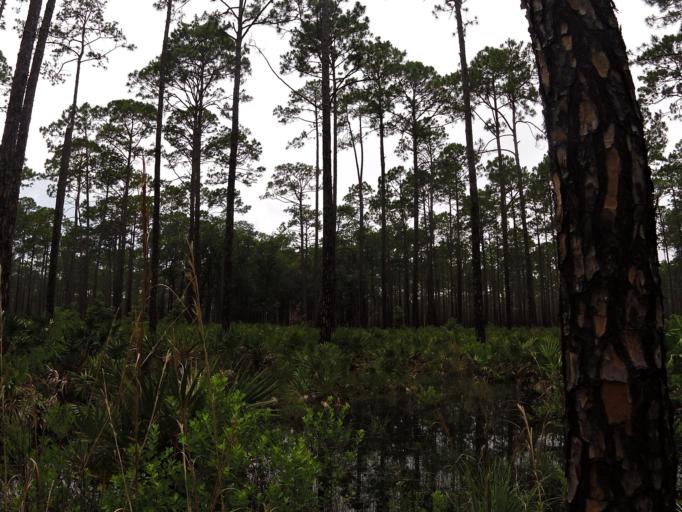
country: US
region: Florida
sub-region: Clay County
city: Green Cove Springs
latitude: 29.9662
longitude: -81.6299
